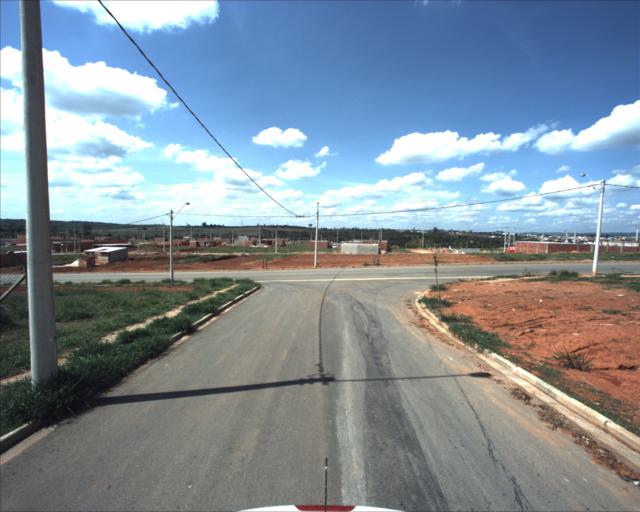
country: BR
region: Sao Paulo
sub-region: Sorocaba
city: Sorocaba
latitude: -23.4105
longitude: -47.4079
